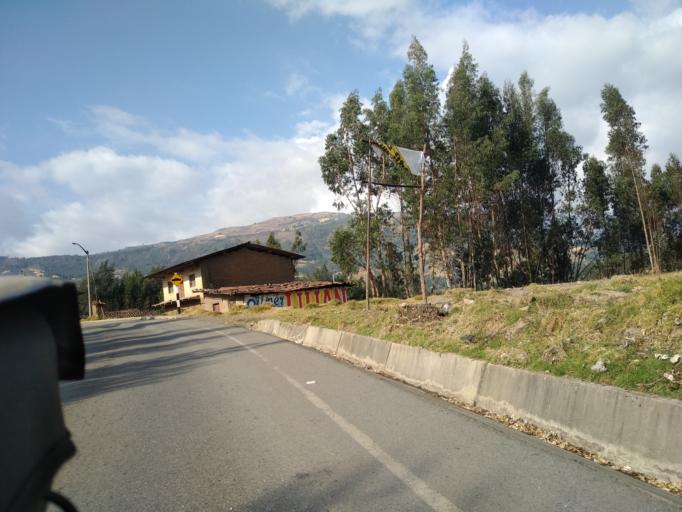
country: PE
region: La Libertad
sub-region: Provincia de Otuzco
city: Agallpampa
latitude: -7.9961
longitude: -78.5207
